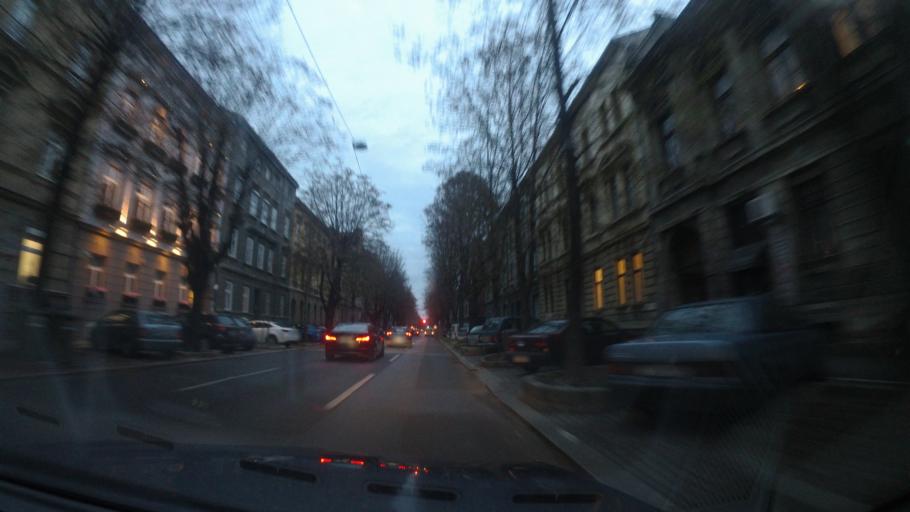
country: HR
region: Grad Zagreb
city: Zagreb - Centar
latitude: 45.8106
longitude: 15.9616
